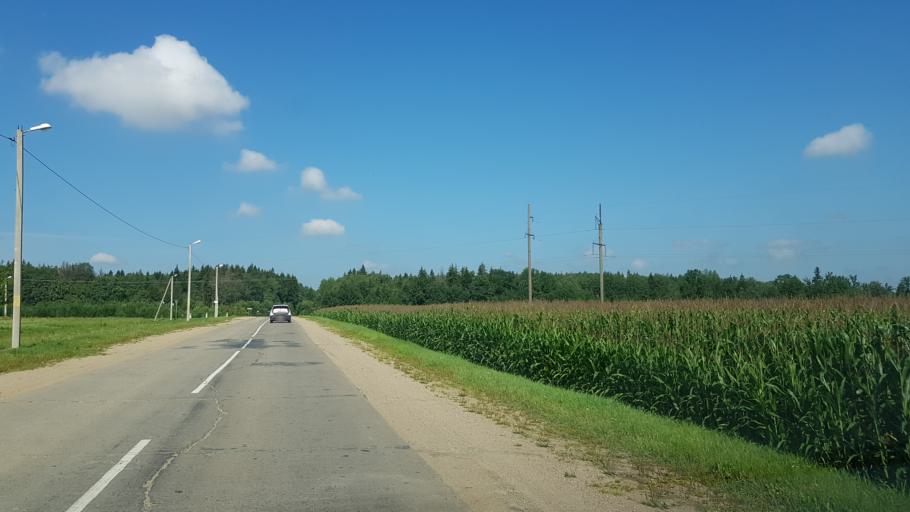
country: BY
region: Minsk
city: Dzyarzhynsk
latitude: 53.7042
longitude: 27.0903
